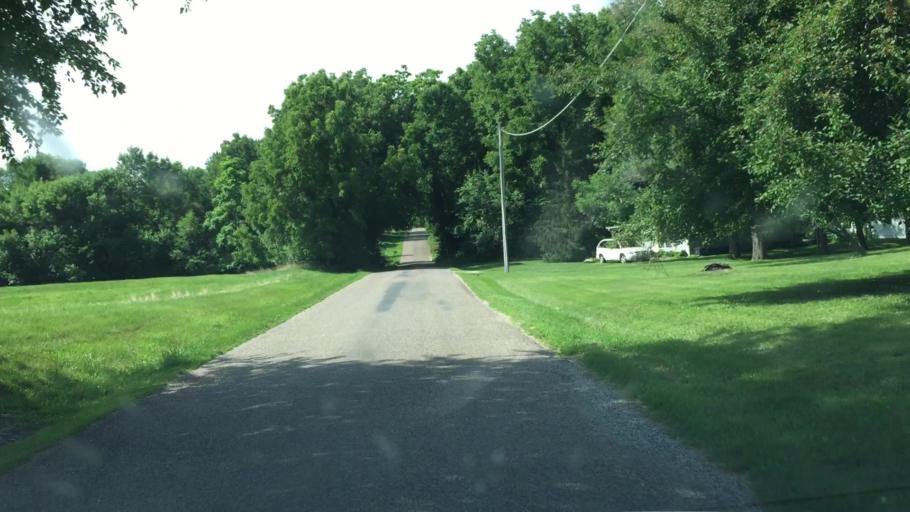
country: US
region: Illinois
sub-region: Hancock County
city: Nauvoo
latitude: 40.5474
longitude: -91.3754
